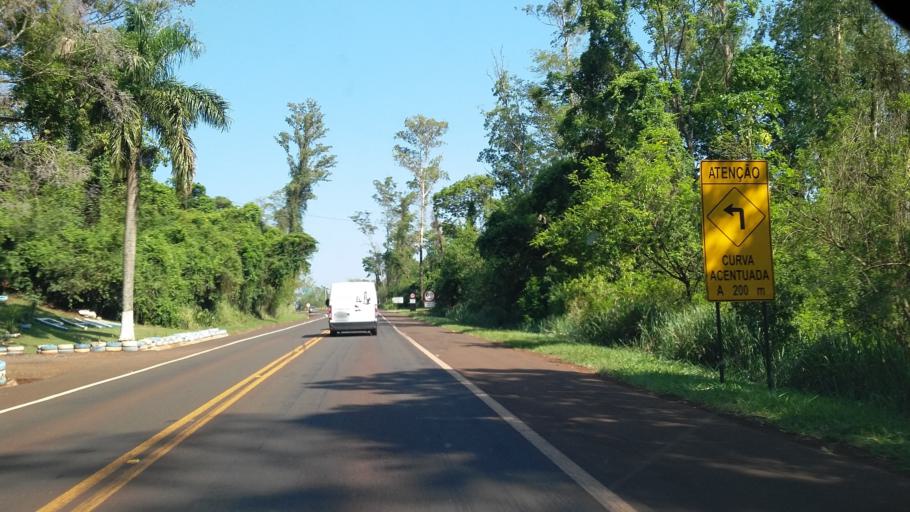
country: BR
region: Parana
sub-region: Bandeirantes
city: Bandeirantes
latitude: -23.1130
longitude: -50.3317
